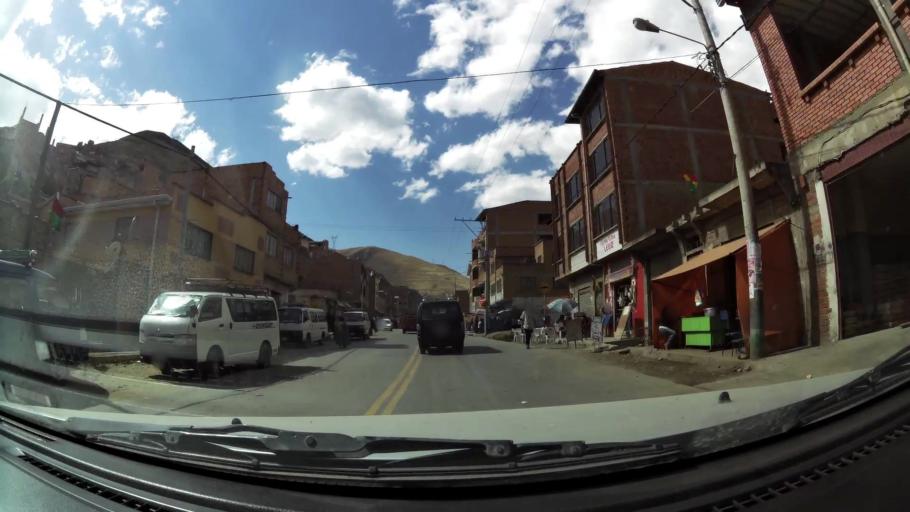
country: BO
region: La Paz
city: La Paz
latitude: -16.4602
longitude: -68.1033
